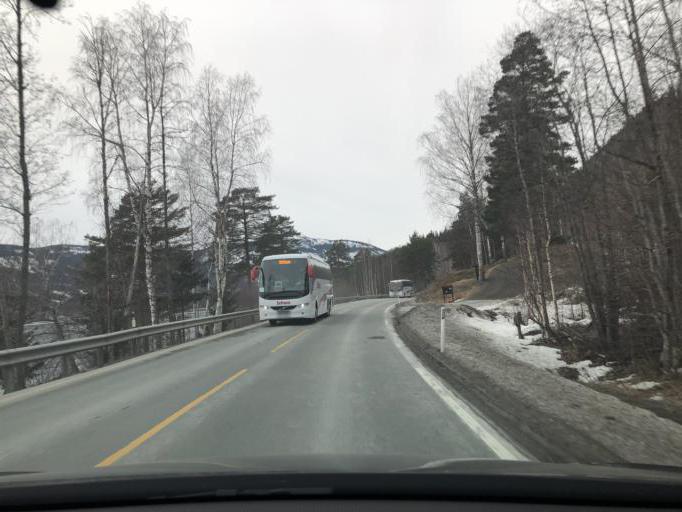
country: NO
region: Buskerud
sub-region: Ringerike
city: Honefoss
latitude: 60.4416
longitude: 10.0867
